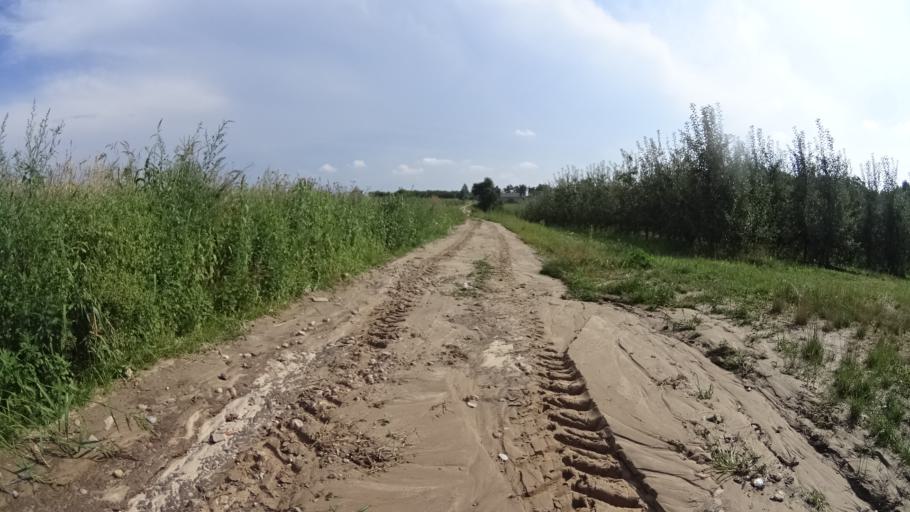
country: PL
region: Masovian Voivodeship
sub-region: Powiat grojecki
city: Goszczyn
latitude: 51.6897
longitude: 20.8393
